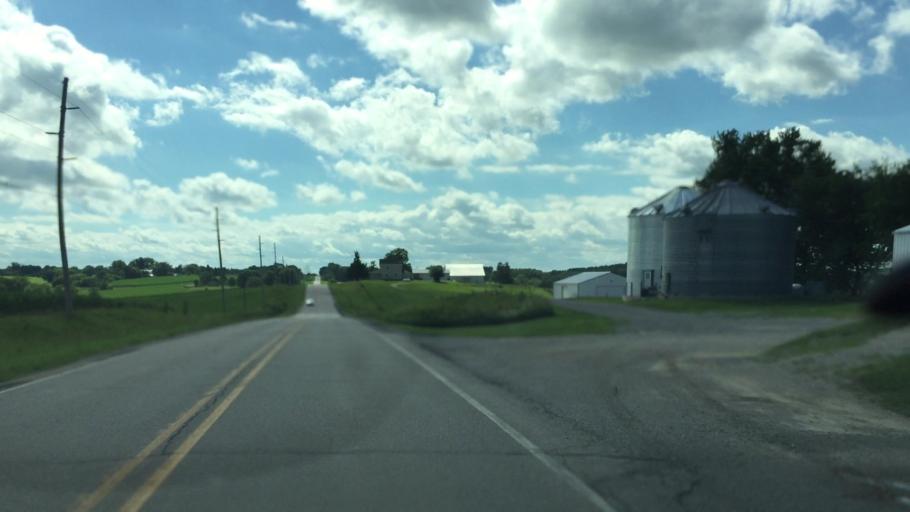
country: US
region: Iowa
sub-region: Linn County
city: Ely
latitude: 41.8475
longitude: -91.5869
